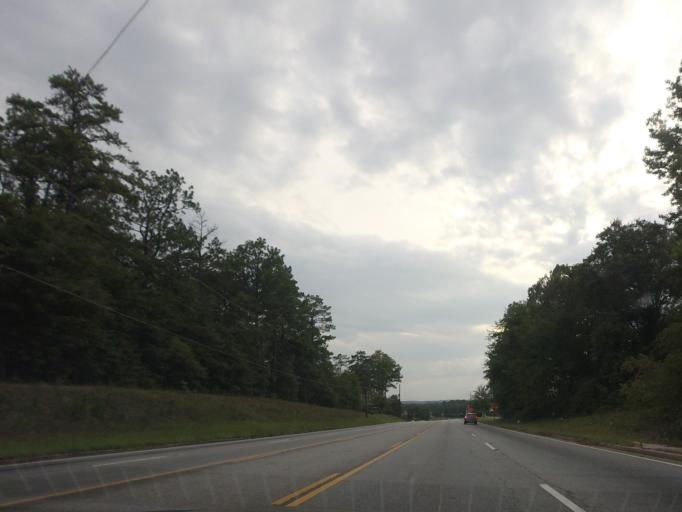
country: US
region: Georgia
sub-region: Bibb County
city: Macon
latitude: 32.8421
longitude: -83.5715
